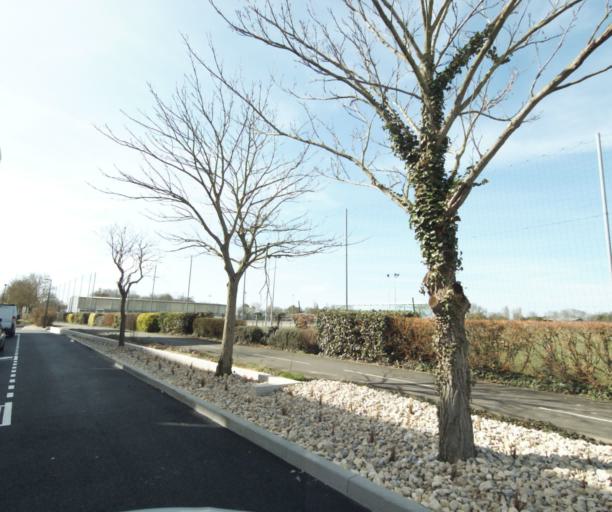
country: FR
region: Poitou-Charentes
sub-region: Departement de la Charente-Maritime
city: La Rochelle
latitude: 46.1736
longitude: -1.1717
